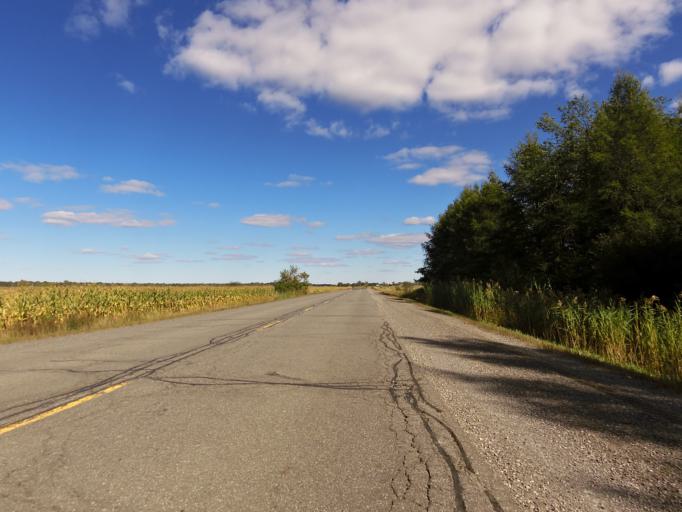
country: CA
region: Ontario
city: Clarence-Rockland
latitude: 45.3363
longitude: -75.4034
